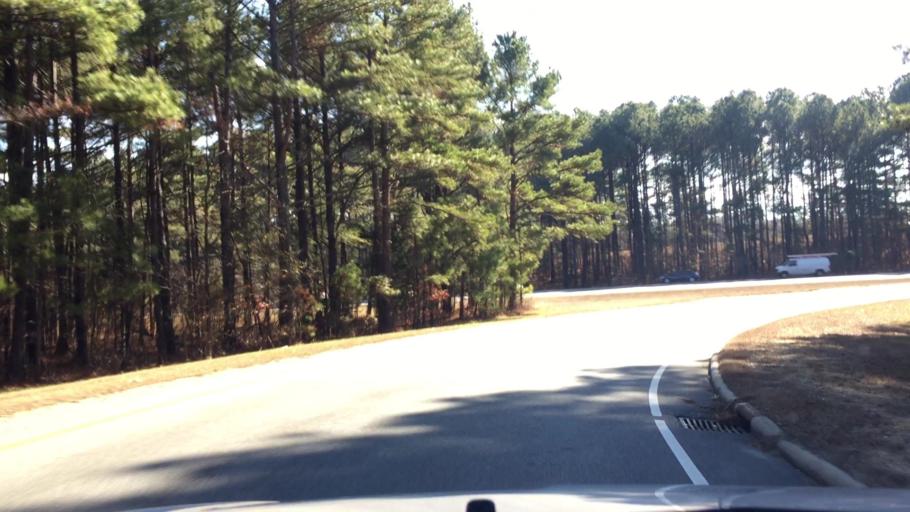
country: US
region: North Carolina
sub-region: Wake County
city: Apex
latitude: 35.7493
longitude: -78.8744
